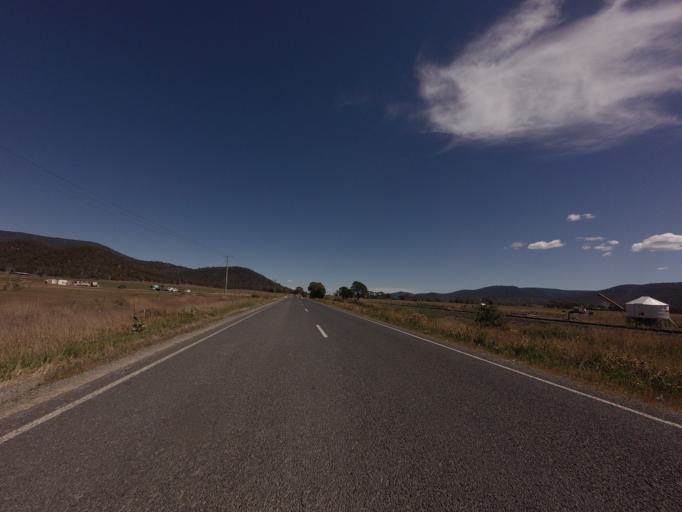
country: AU
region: Tasmania
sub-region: Break O'Day
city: St Helens
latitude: -41.6721
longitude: 147.8999
